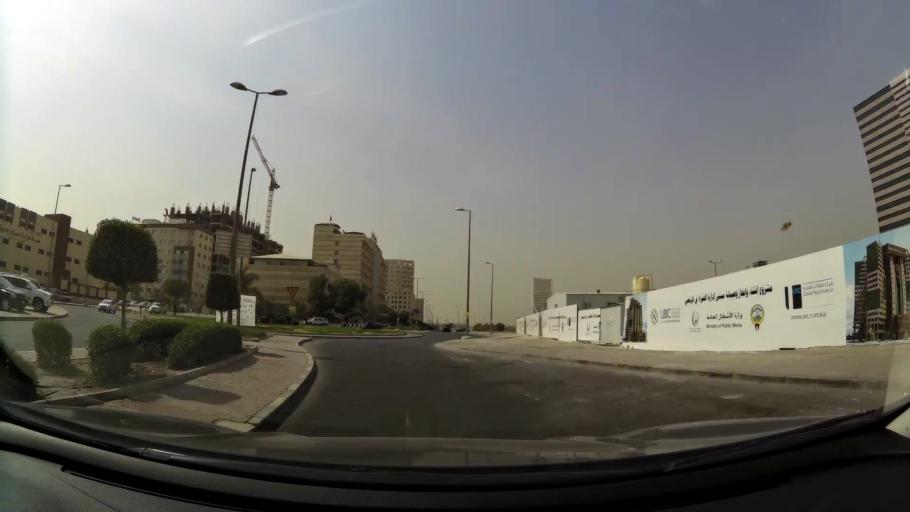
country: KW
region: Al Asimah
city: Ar Rabiyah
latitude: 29.3027
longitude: 47.9129
